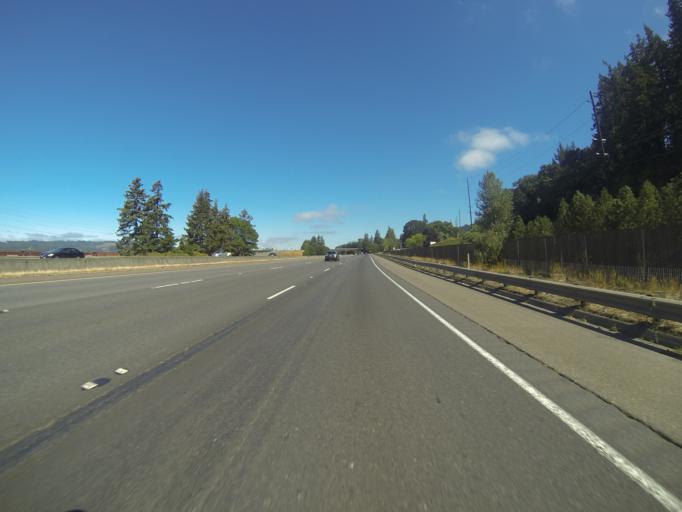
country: US
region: Washington
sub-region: Cowlitz County
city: Kalama
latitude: 46.0152
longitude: -122.8486
